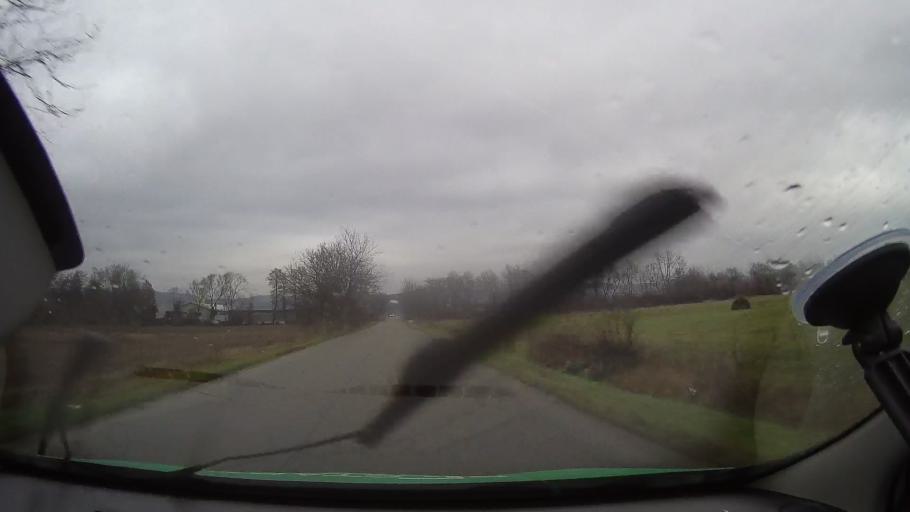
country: RO
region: Hunedoara
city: Vata de Jos
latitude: 46.1852
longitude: 22.6057
